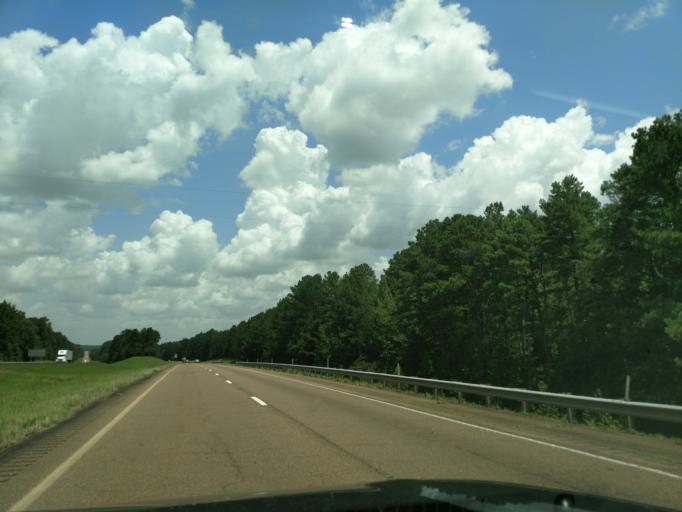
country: US
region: Mississippi
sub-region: Montgomery County
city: Winona
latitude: 33.5011
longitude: -89.7656
